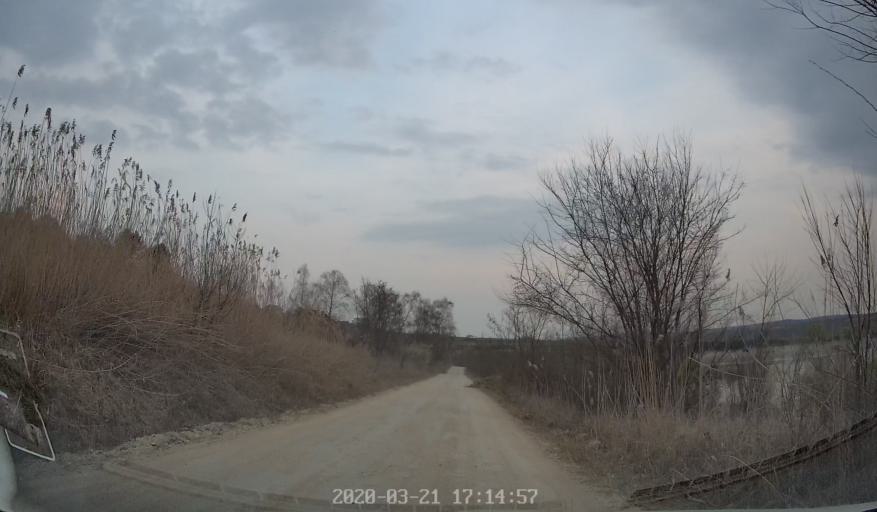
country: MD
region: Laloveni
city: Ialoveni
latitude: 46.9593
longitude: 28.7435
